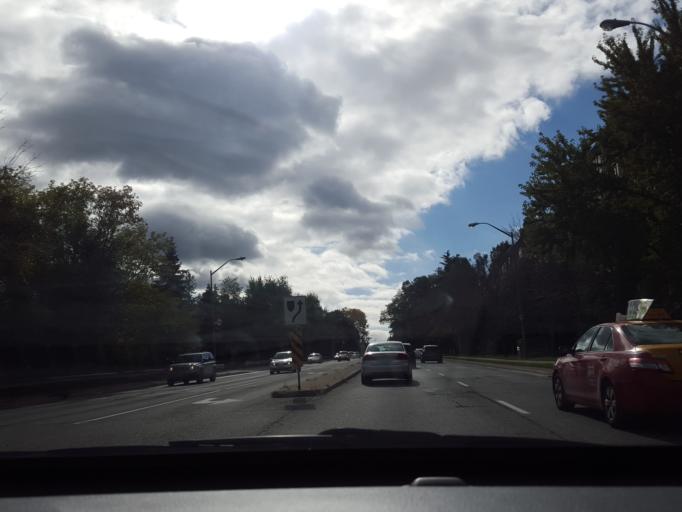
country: CA
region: Ontario
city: Willowdale
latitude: 43.7387
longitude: -79.4058
